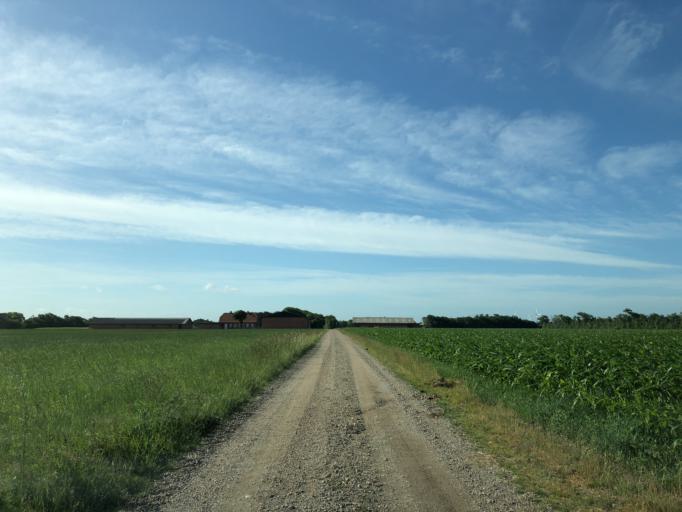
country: DK
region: Central Jutland
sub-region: Holstebro Kommune
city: Ulfborg
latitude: 56.3357
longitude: 8.3020
